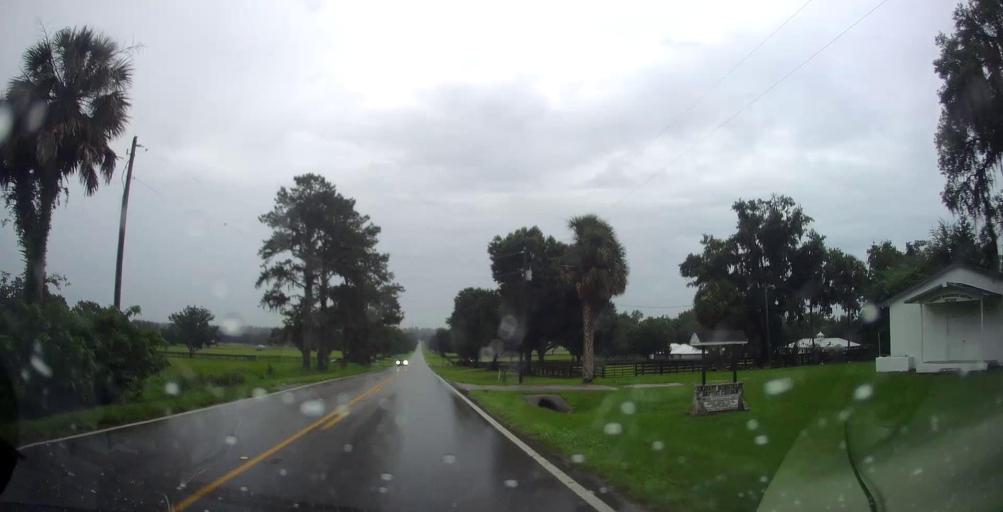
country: US
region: Florida
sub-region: Marion County
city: Citra
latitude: 29.3583
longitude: -82.2449
